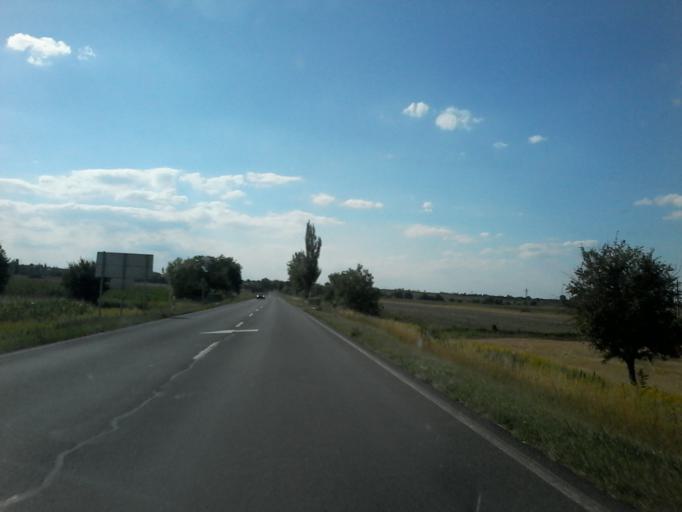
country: HU
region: Vas
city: Janoshaza
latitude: 47.1567
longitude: 17.0702
